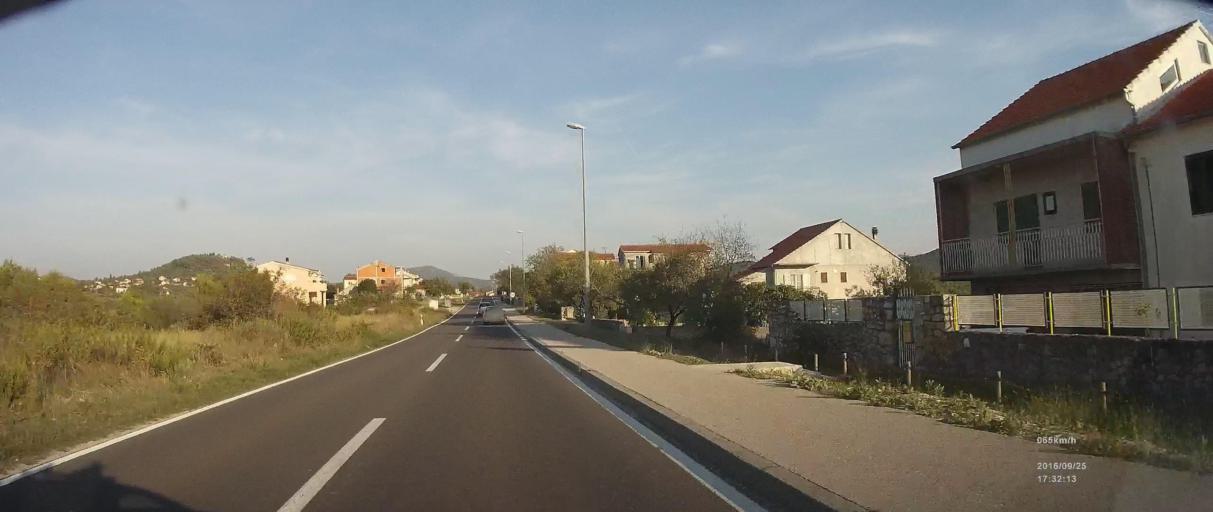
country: HR
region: Sibensko-Kniniska
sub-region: Grad Sibenik
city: Brodarica
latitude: 43.6754
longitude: 15.9995
